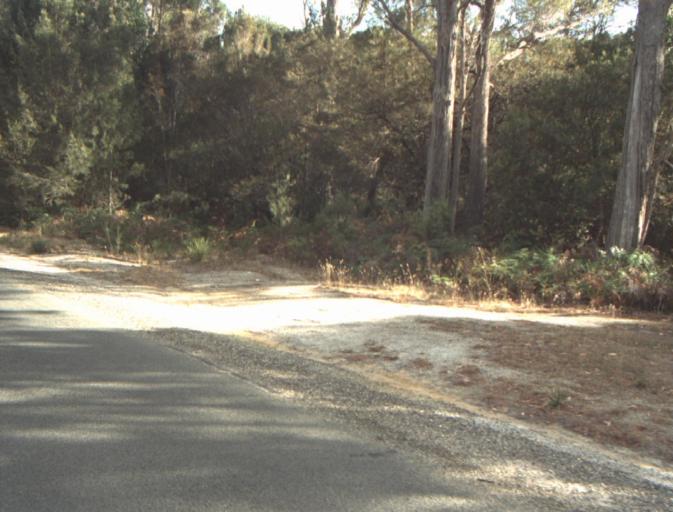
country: AU
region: Tasmania
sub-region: Dorset
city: Bridport
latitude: -41.1269
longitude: 147.2112
